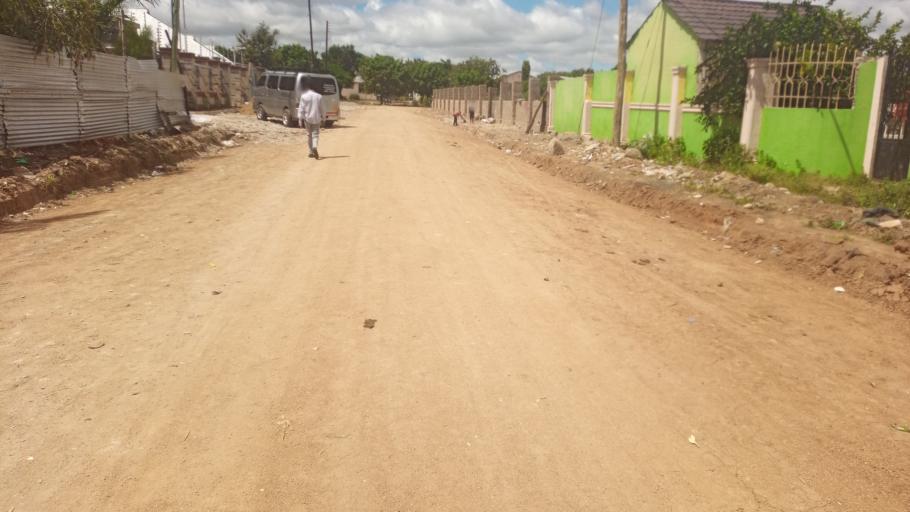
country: TZ
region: Dodoma
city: Kisasa
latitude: -6.1788
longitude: 35.7659
